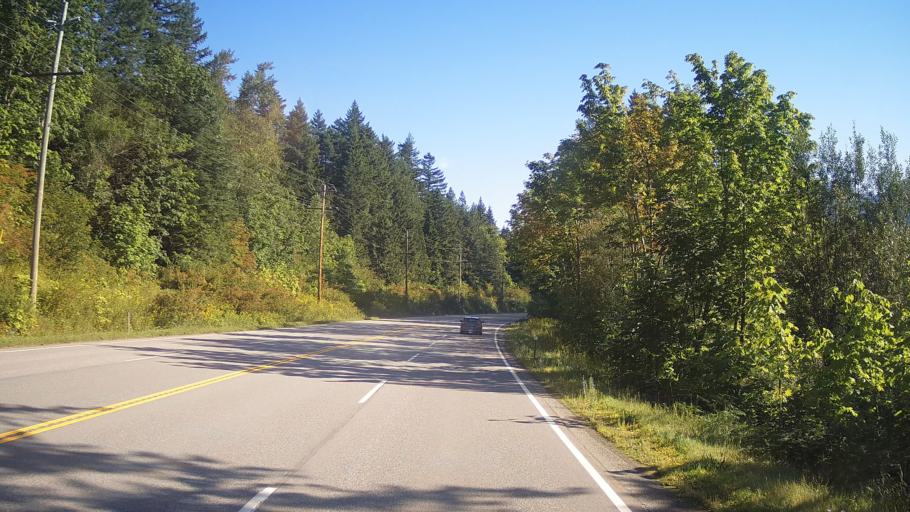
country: CA
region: British Columbia
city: Hope
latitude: 49.4607
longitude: -121.4351
